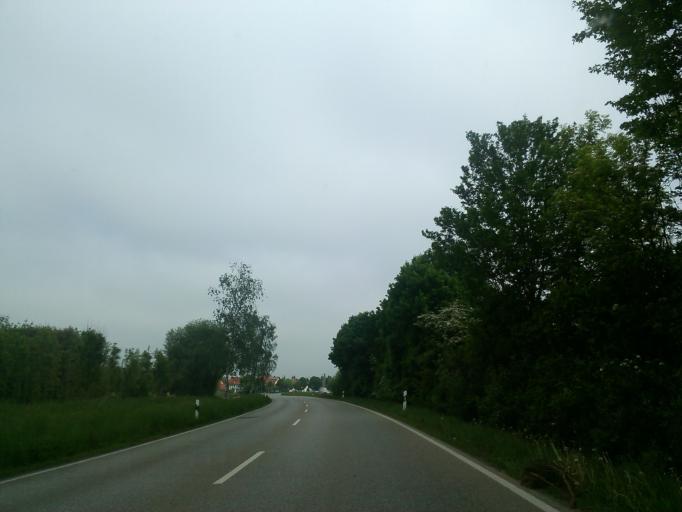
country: DE
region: Bavaria
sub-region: Upper Bavaria
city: Olching
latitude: 48.1873
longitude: 11.3290
